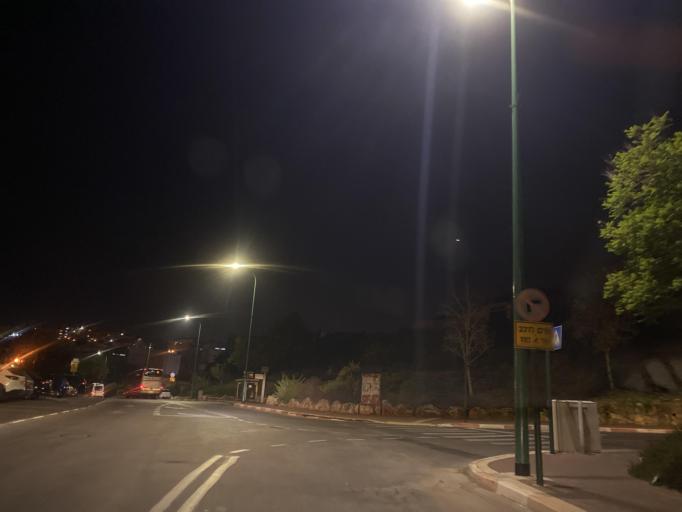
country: IL
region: Haifa
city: Daliyat el Karmil
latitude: 32.6457
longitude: 35.0900
